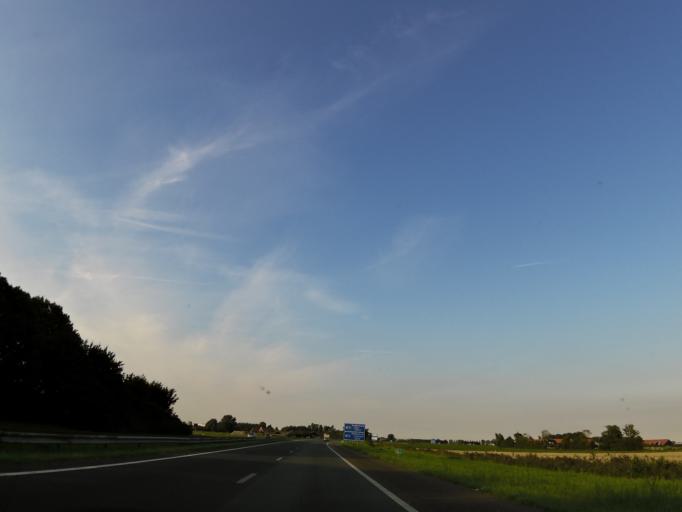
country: NL
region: Zeeland
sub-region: Gemeente Middelburg
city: Middelburg
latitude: 51.4664
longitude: 3.6149
